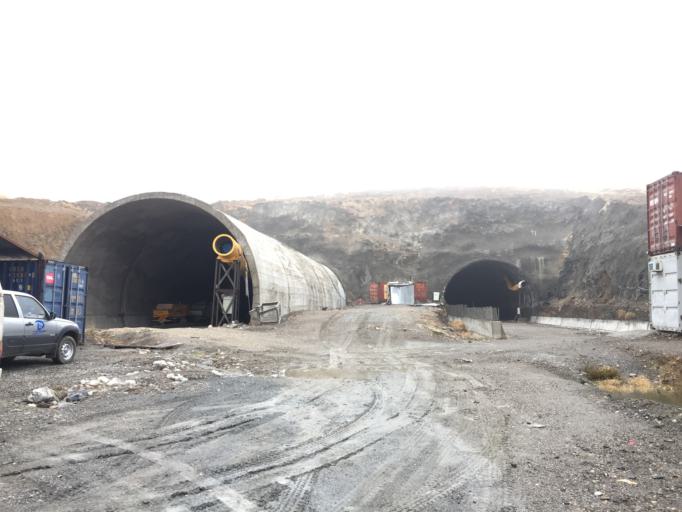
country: KZ
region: Ongtustik Qazaqstan
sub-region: Tulkibas Audany
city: Zhabagly
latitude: 42.5176
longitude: 70.5660
